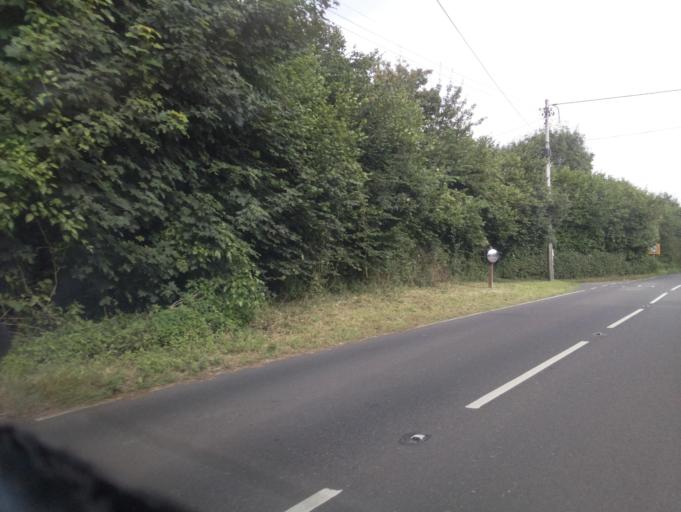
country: GB
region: England
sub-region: Bath and North East Somerset
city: Chew Magna
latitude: 51.3463
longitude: -2.6338
